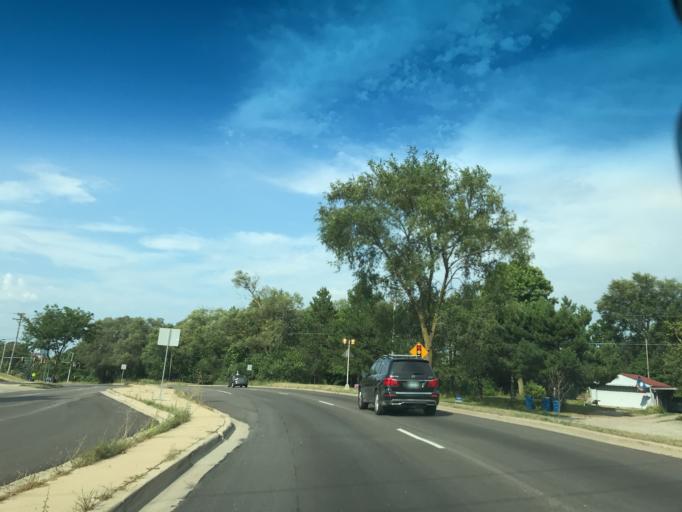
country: US
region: Michigan
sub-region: Washtenaw County
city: Ann Arbor
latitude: 42.2553
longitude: -83.7509
